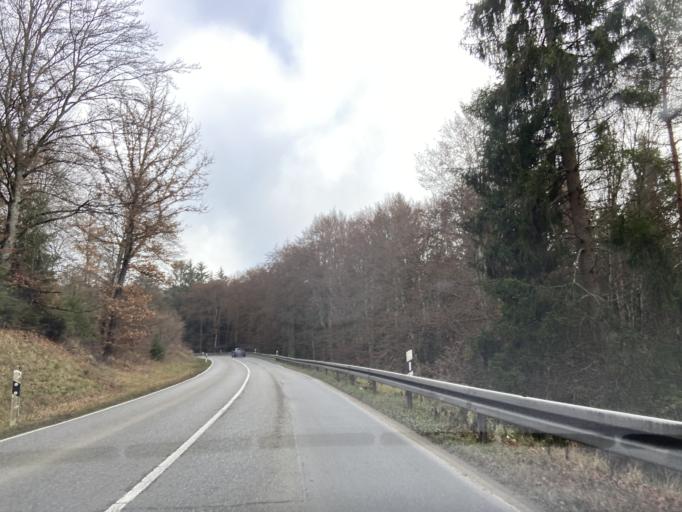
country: DE
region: Baden-Wuerttemberg
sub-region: Tuebingen Region
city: Neufra
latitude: 48.2436
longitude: 9.1935
